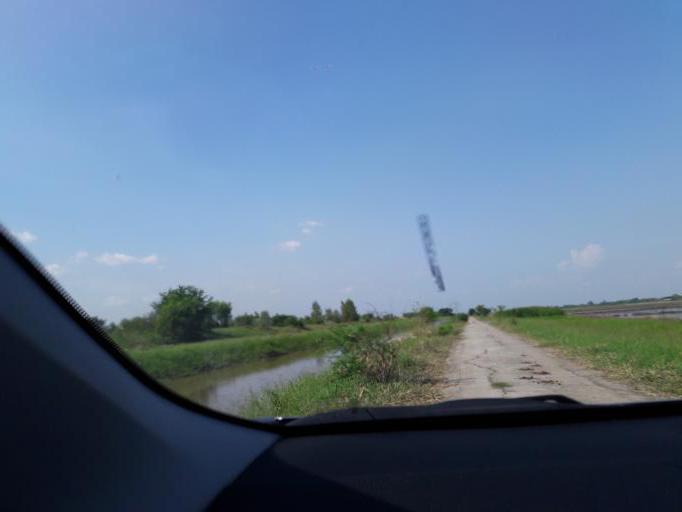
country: TH
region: Ang Thong
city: Ang Thong
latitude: 14.5490
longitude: 100.4067
